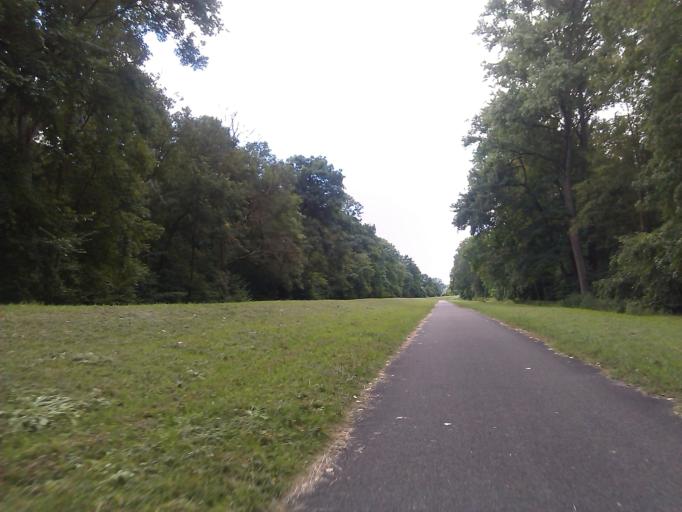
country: DE
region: Rheinland-Pfalz
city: Altrip
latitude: 49.4116
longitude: 8.4942
